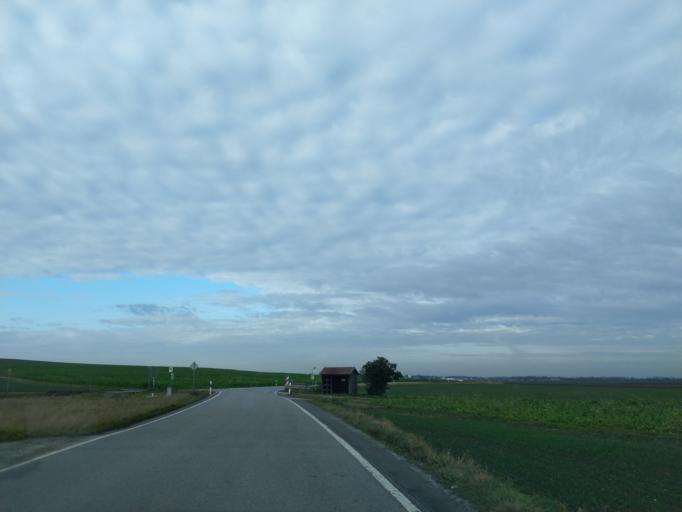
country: DE
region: Bavaria
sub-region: Lower Bavaria
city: Wallerfing
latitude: 48.6914
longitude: 12.8535
